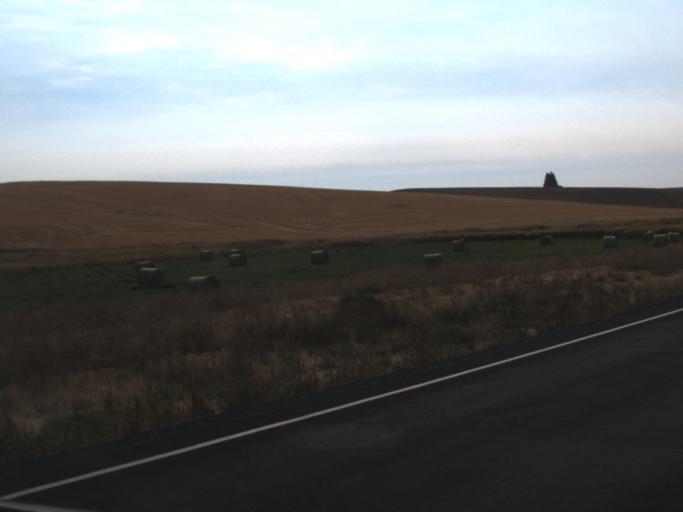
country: US
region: Washington
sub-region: Whitman County
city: Pullman
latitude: 46.8761
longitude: -117.1268
